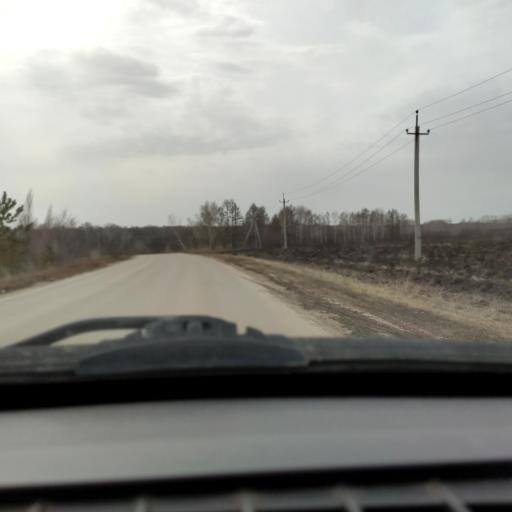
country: RU
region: Samara
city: Dubovyy Umet
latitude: 53.0408
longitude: 50.1752
